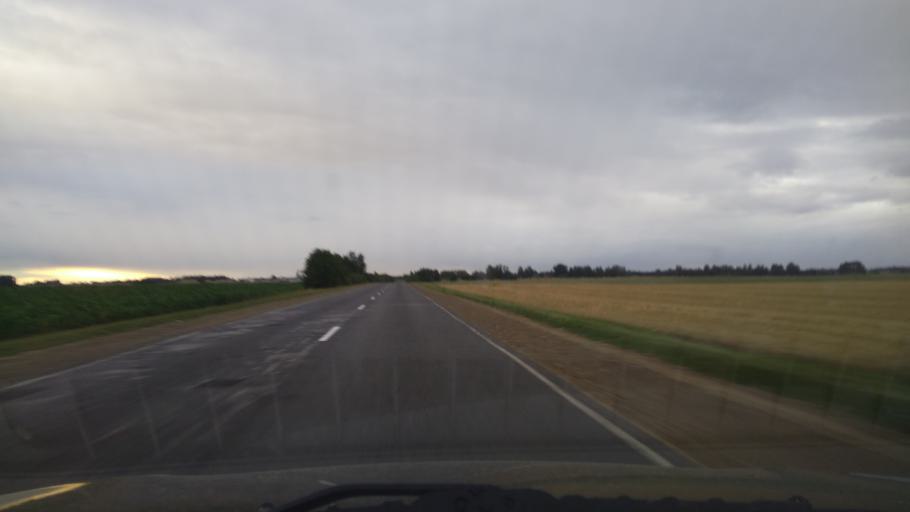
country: BY
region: Brest
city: Byaroza
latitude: 52.4419
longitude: 24.9755
